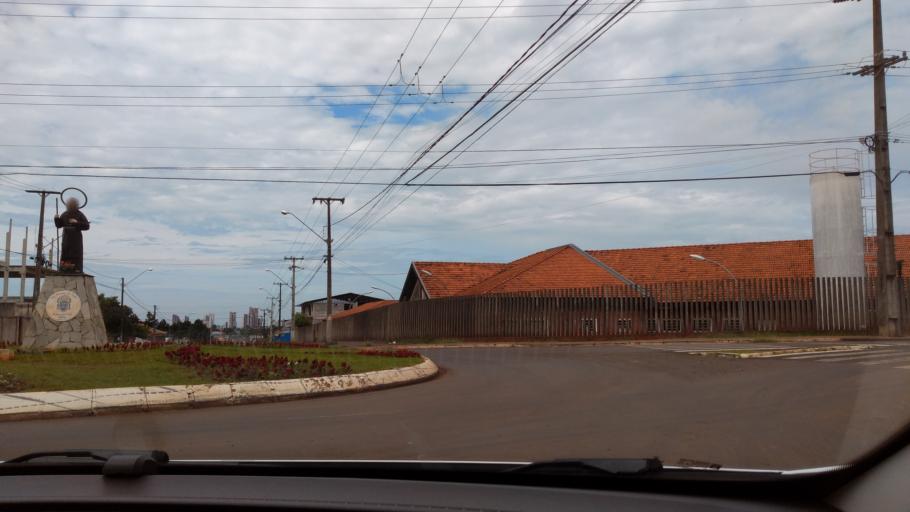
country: BR
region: Parana
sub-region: Guarapuava
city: Guarapuava
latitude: -25.3734
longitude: -51.4439
